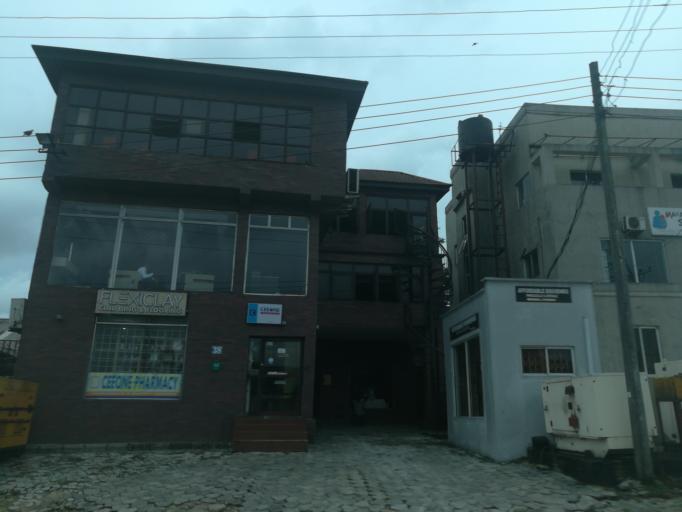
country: NG
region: Rivers
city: Port Harcourt
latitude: 4.8153
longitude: 6.9988
